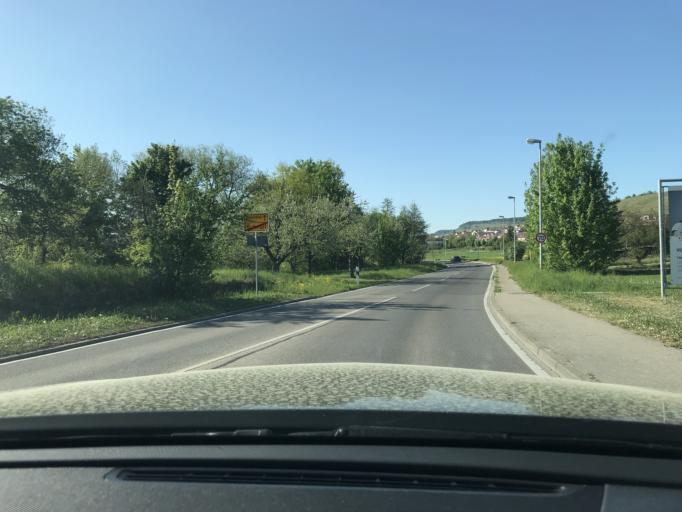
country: DE
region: Baden-Wuerttemberg
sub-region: Regierungsbezirk Stuttgart
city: Weinstadt-Endersbach
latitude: 48.7958
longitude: 9.3979
